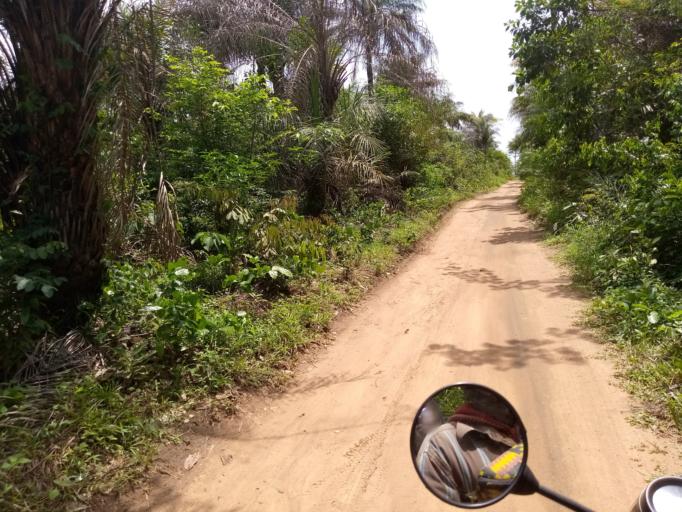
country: SL
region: Western Area
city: Waterloo
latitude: 8.3720
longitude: -13.0000
